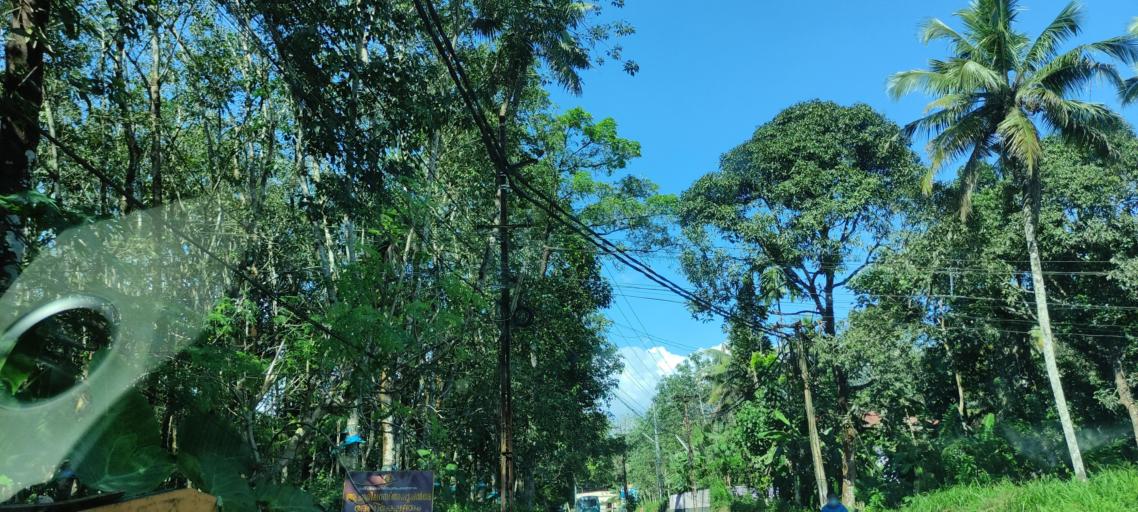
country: IN
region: Kerala
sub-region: Pattanamtitta
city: Adur
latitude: 9.1694
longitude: 76.7415
